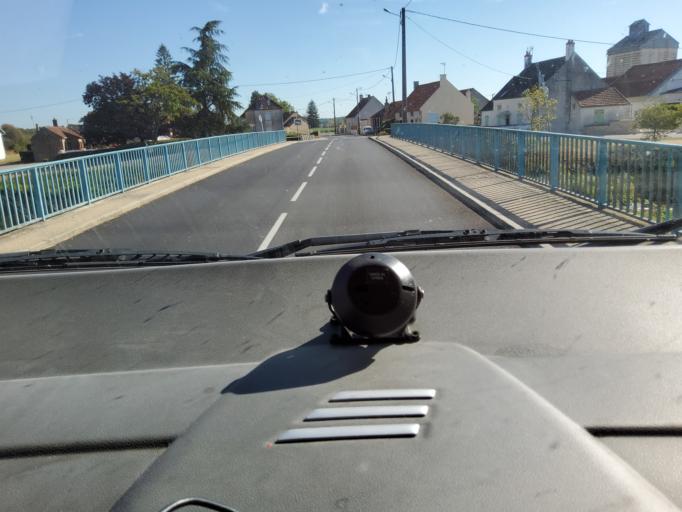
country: FR
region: Bourgogne
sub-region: Departement de la Cote-d'Or
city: Auxonne
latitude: 47.1377
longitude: 5.3425
